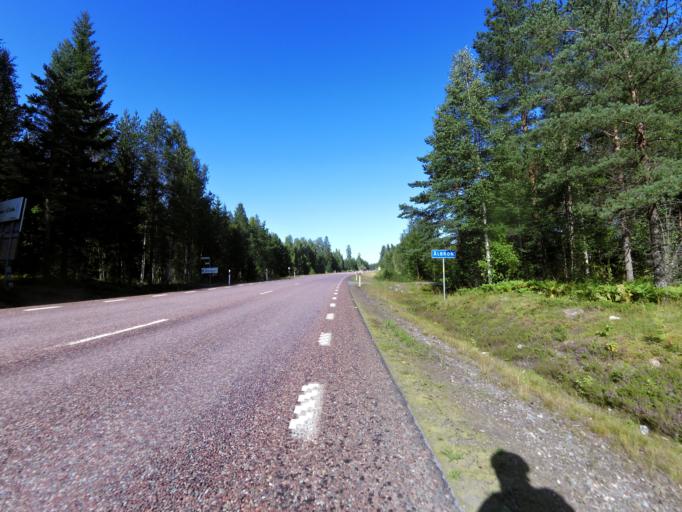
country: SE
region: Gaevleborg
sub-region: Hofors Kommun
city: Hofors
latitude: 60.5549
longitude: 16.4784
